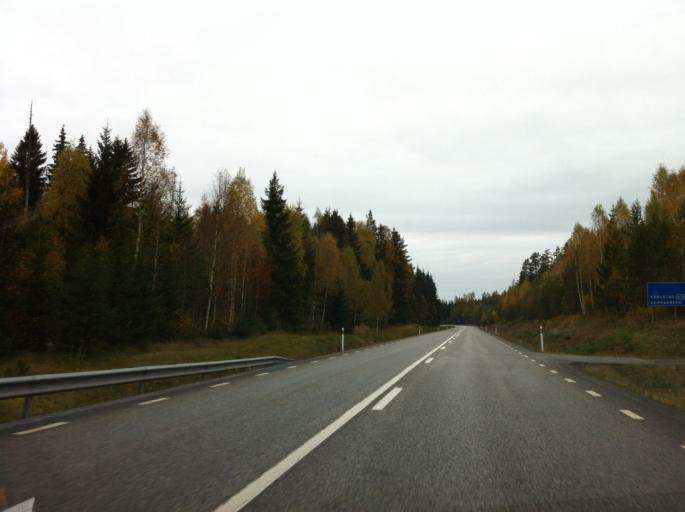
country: SE
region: OErebro
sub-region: Ljusnarsbergs Kommun
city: Kopparberg
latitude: 59.8656
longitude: 15.0570
